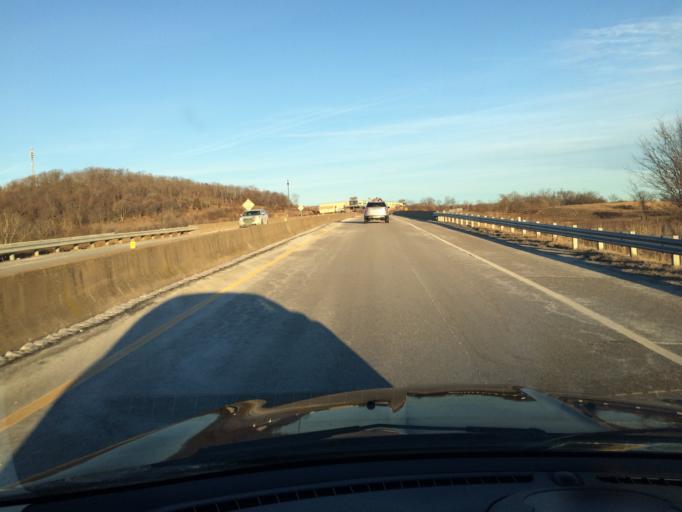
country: US
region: Virginia
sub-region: Augusta County
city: Jolivue
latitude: 38.1073
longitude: -79.0605
